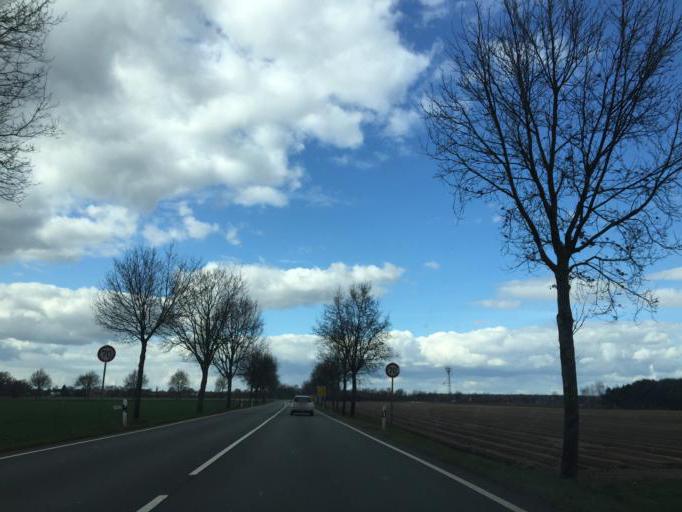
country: DE
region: Lower Saxony
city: Broeckel
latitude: 52.5066
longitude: 10.2292
